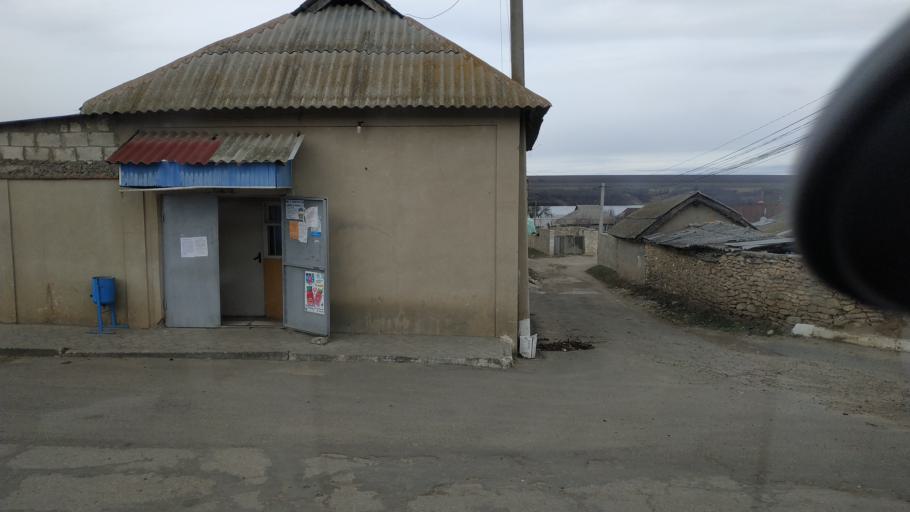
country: MD
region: Telenesti
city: Cocieri
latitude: 47.3858
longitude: 29.1130
